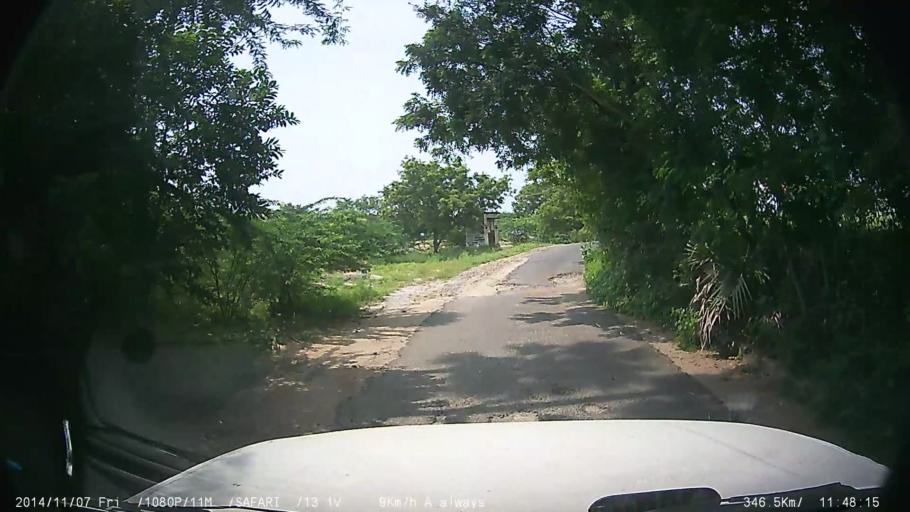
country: IN
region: Tamil Nadu
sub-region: Tiruppur
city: Avinashi
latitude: 11.1657
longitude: 77.2692
